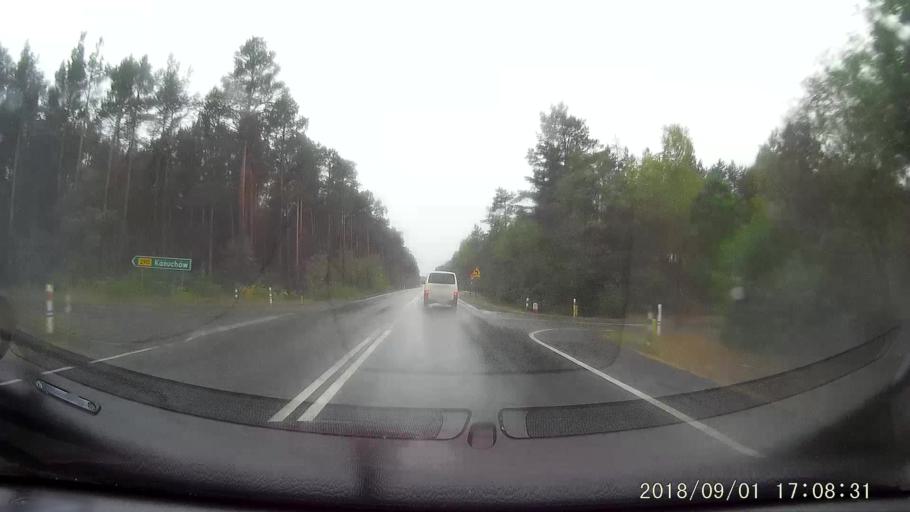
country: PL
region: Lubusz
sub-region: Powiat zielonogorski
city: Nowogrod Bobrzanski
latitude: 51.8287
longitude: 15.3073
